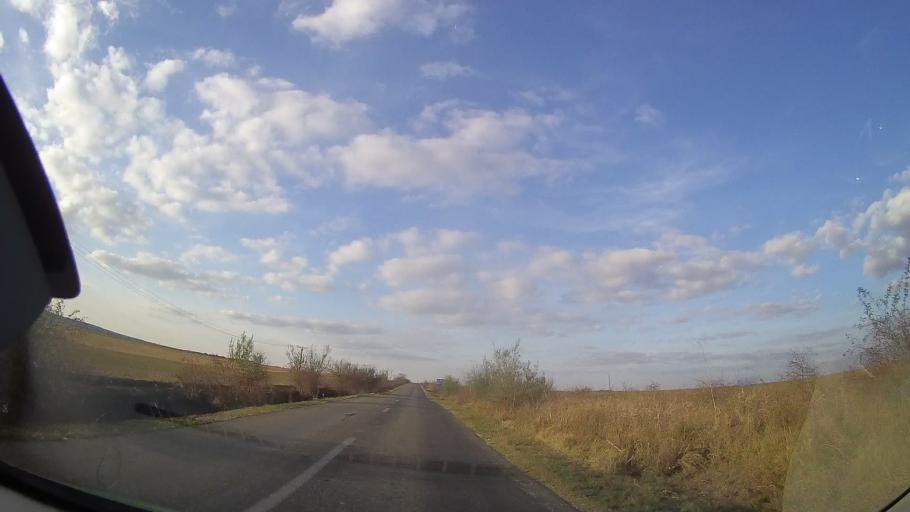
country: RO
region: Constanta
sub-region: Comuna Dumbraveni
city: Dumbraveni
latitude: 43.9303
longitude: 28.0280
